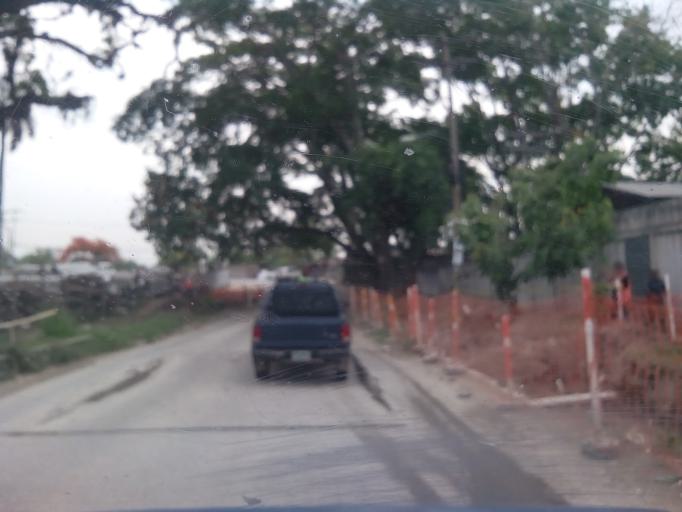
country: HN
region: Cortes
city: San Pedro Sula
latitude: 15.4999
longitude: -87.9855
